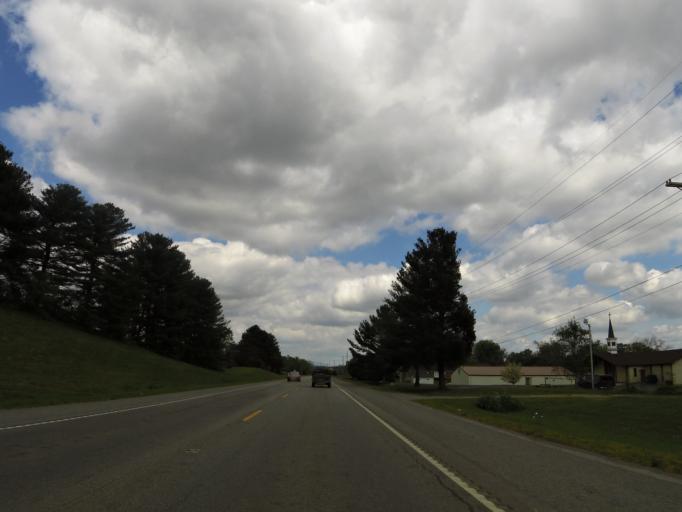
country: US
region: Kentucky
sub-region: Bell County
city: Middlesboro
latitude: 36.4900
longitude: -83.8240
